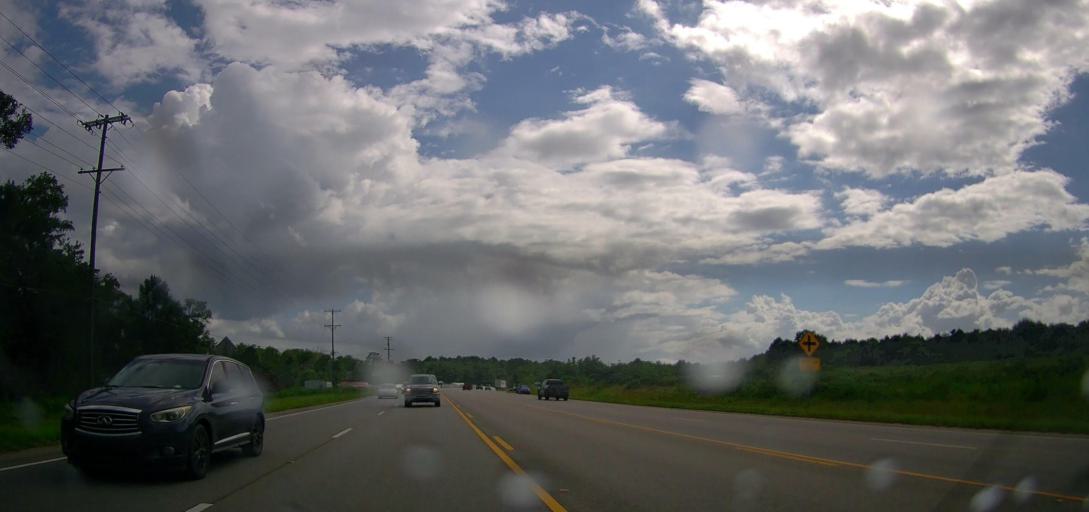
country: US
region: Georgia
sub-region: Coffee County
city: Douglas
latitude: 31.4935
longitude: -82.8307
